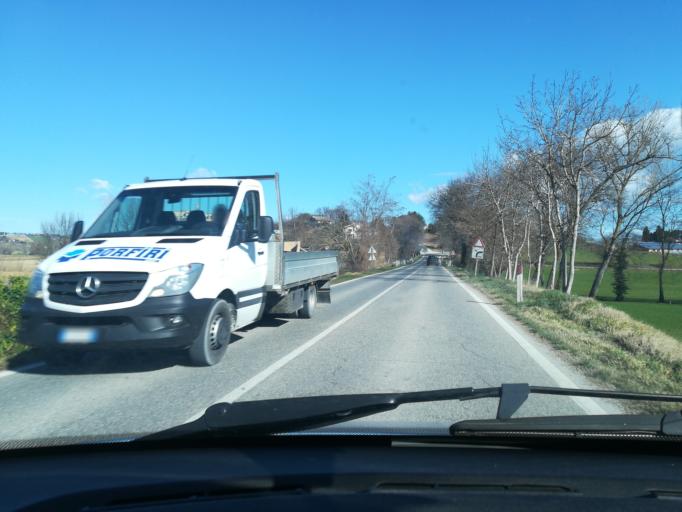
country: IT
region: The Marches
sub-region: Provincia di Macerata
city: Montecassiano
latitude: 43.3514
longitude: 13.4367
